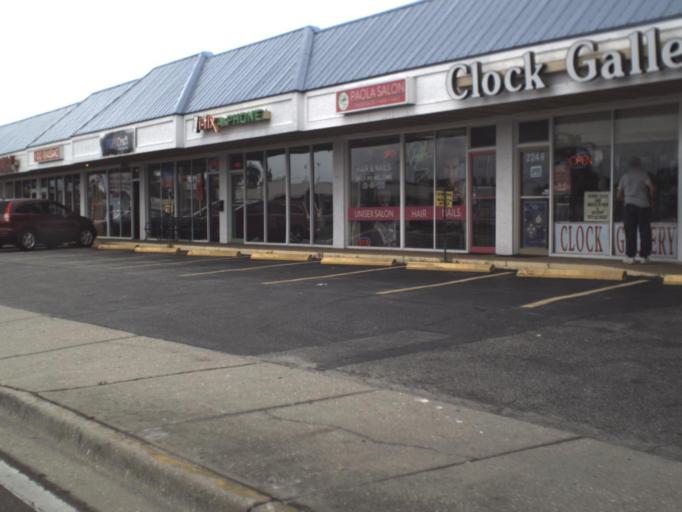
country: US
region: Florida
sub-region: Sarasota County
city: South Sarasota
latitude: 27.2989
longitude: -82.5244
